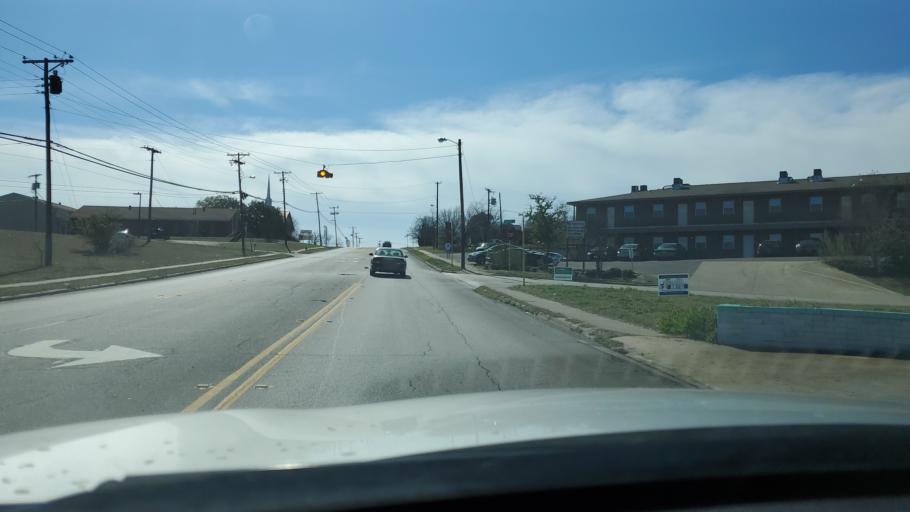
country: US
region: Texas
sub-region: Bell County
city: Killeen
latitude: 31.1105
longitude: -97.7286
